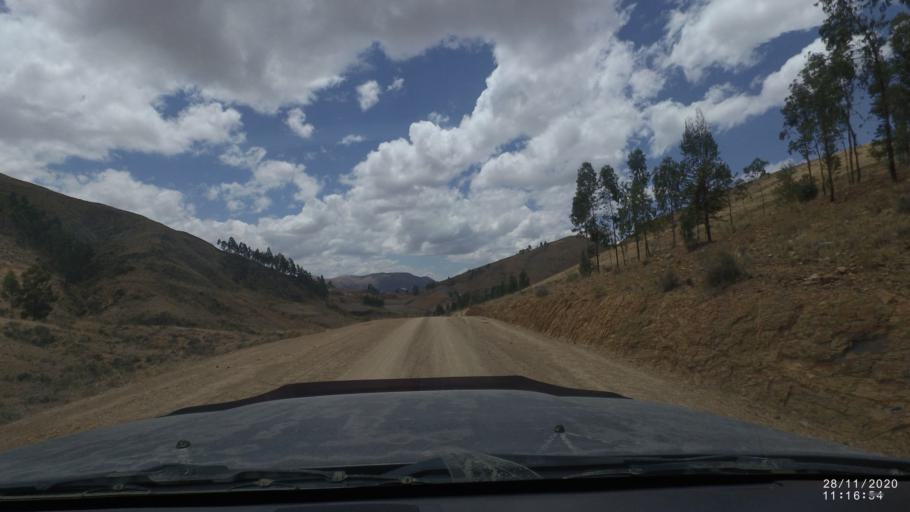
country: BO
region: Cochabamba
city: Tarata
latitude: -17.7495
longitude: -66.0805
